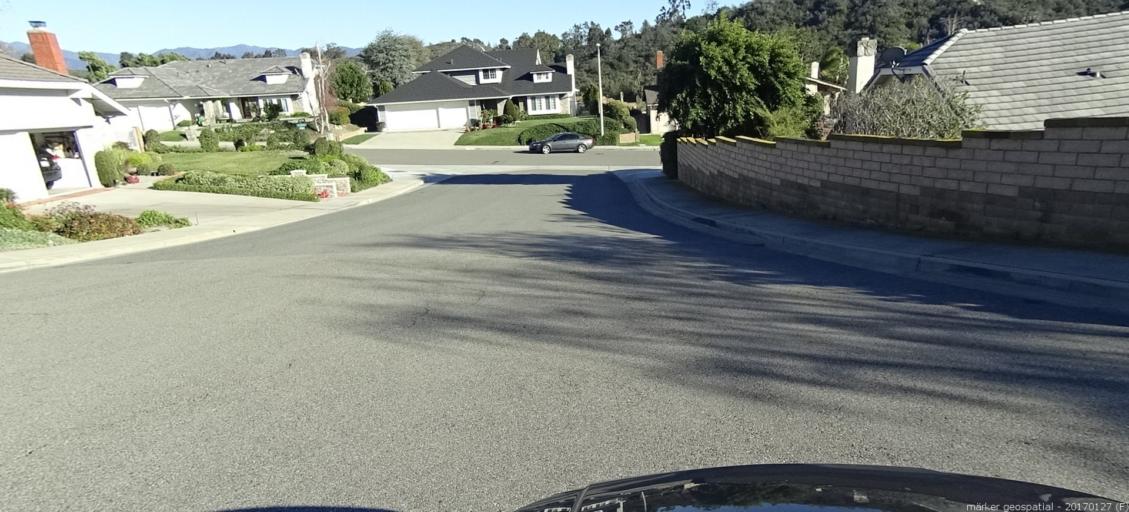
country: US
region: California
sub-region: Orange County
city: Lake Forest
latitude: 33.6493
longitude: -117.6644
